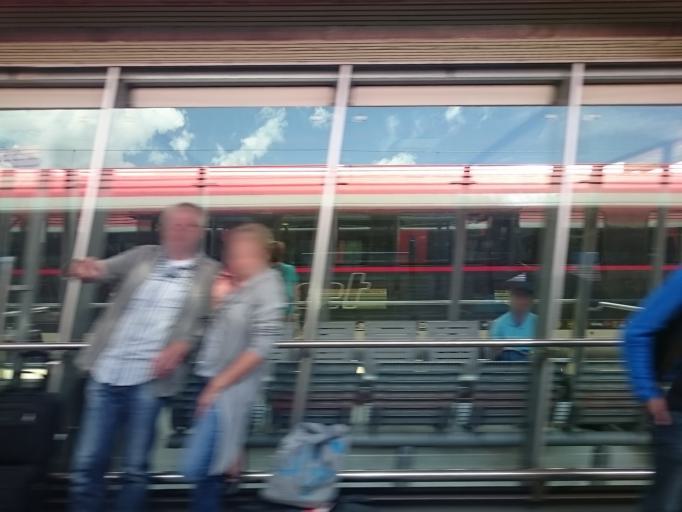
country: AT
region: Tyrol
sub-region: Innsbruck Stadt
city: Innsbruck
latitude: 47.2630
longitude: 11.4011
